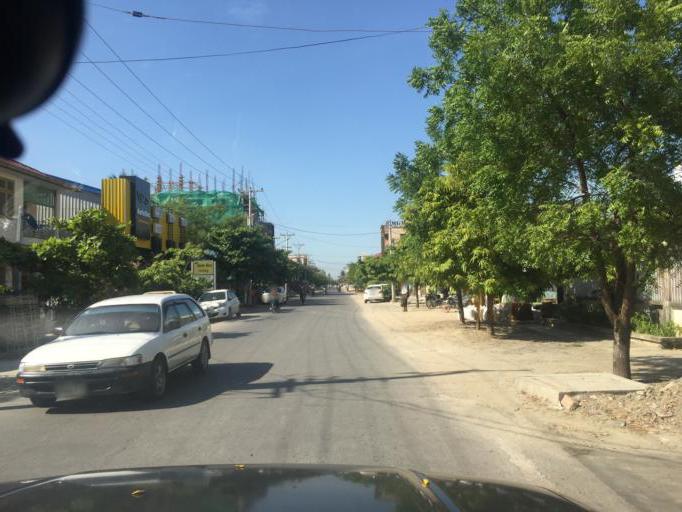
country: MM
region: Mandalay
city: Mandalay
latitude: 21.9603
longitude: 96.1101
